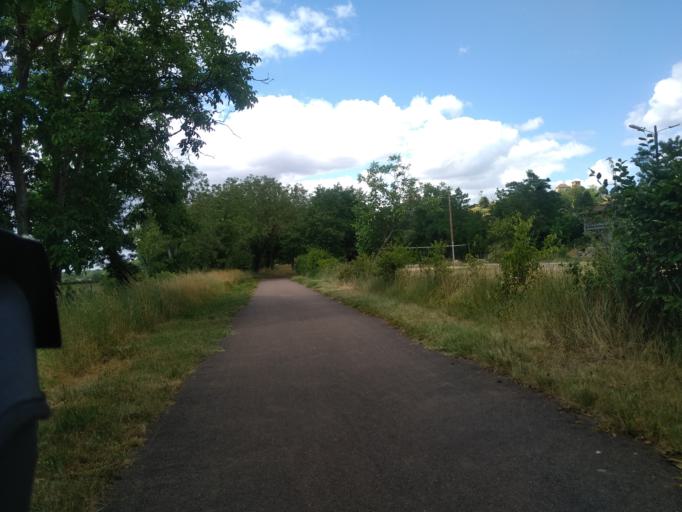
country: FR
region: Rhone-Alpes
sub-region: Departement de la Loire
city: Briennon
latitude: 46.2032
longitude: 4.0780
